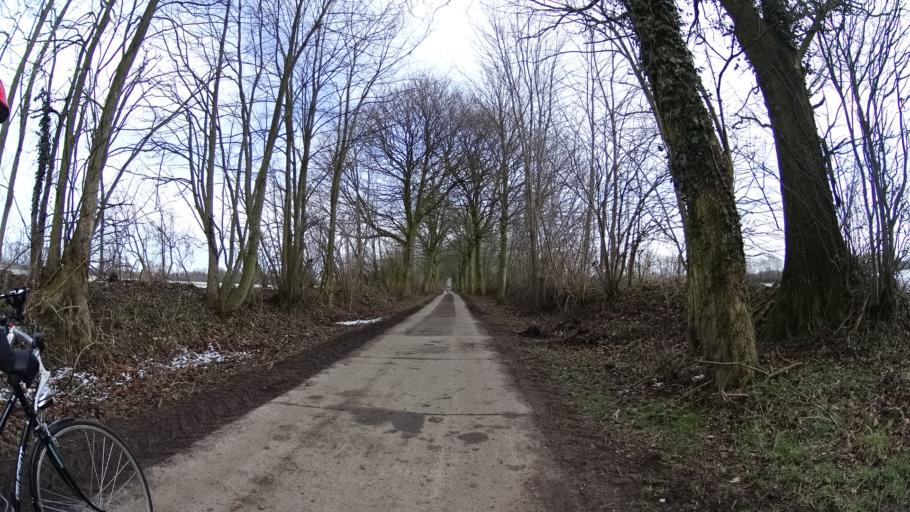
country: DE
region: Schleswig-Holstein
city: Gonnebek
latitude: 54.0651
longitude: 10.1739
